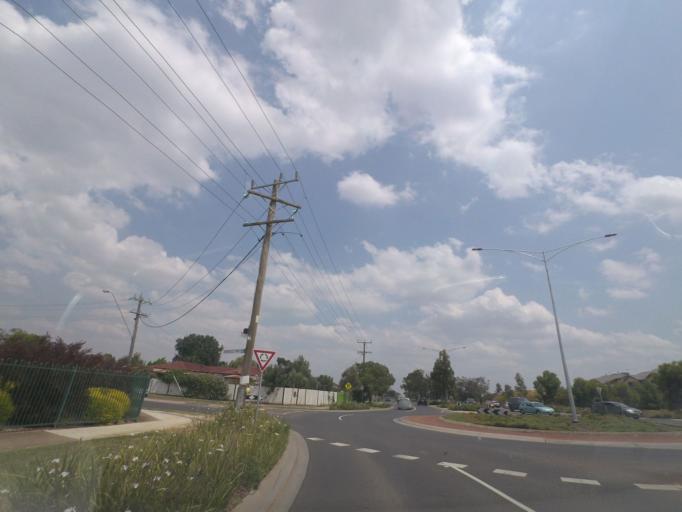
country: AU
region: Victoria
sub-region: Melton
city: Melton West
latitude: -37.6740
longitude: 144.5787
